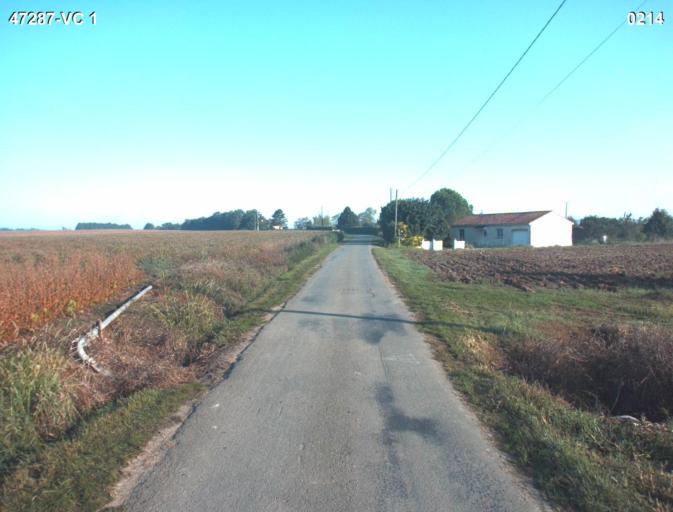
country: FR
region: Aquitaine
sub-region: Departement du Lot-et-Garonne
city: Laplume
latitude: 44.1253
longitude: 0.4573
